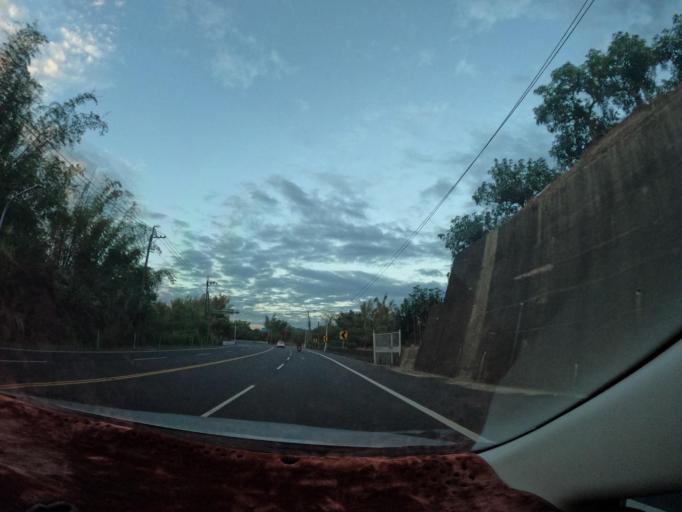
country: TW
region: Taiwan
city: Yujing
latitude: 23.0712
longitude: 120.4240
